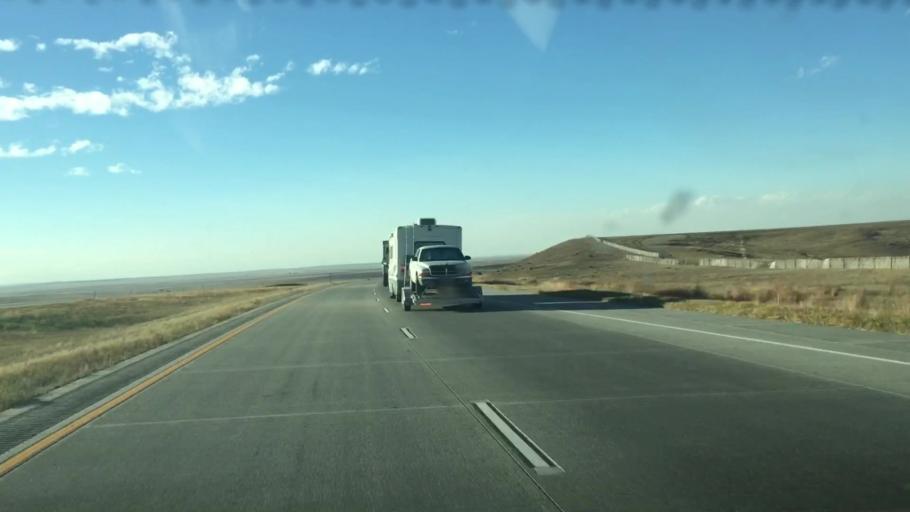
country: US
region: Colorado
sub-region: Lincoln County
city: Limon
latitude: 39.3579
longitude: -103.8724
